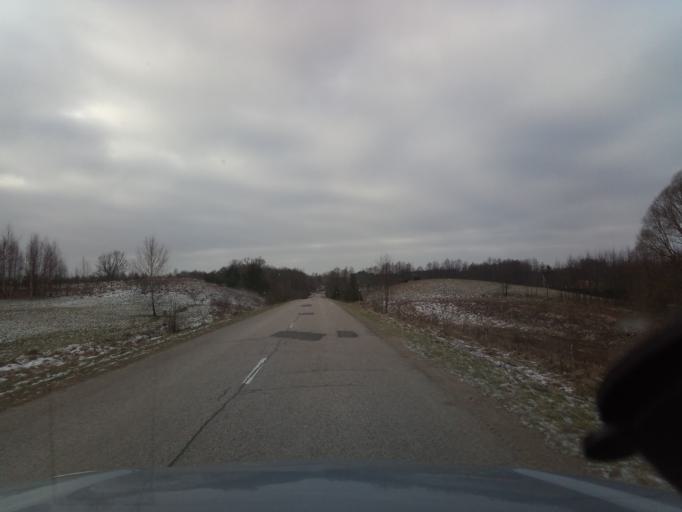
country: LT
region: Alytaus apskritis
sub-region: Alytaus rajonas
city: Daugai
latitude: 54.3478
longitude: 24.3177
